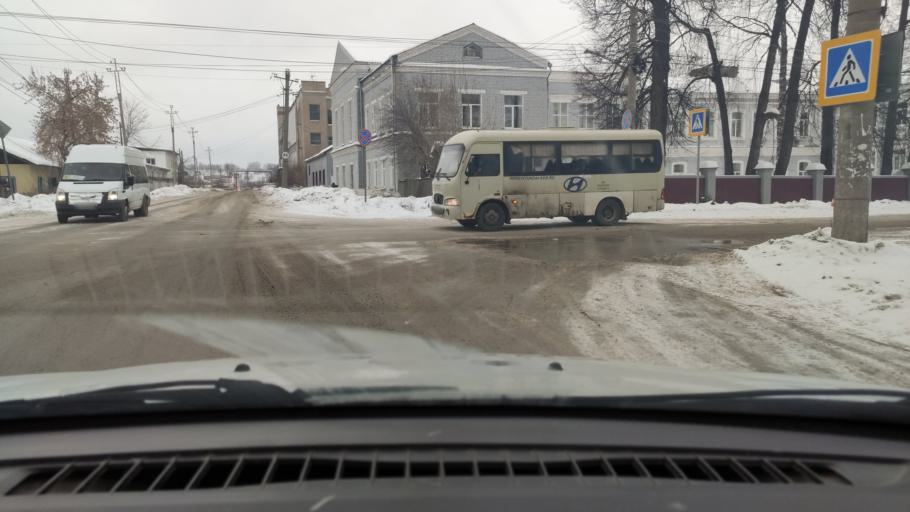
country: RU
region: Perm
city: Kungur
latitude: 57.4407
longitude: 56.9290
